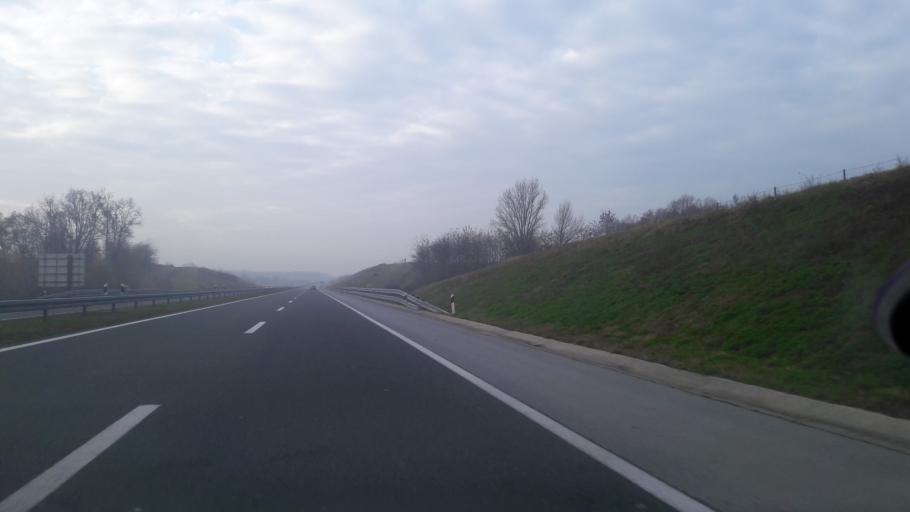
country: HR
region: Osjecko-Baranjska
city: Piskorevci
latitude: 45.2977
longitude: 18.3608
